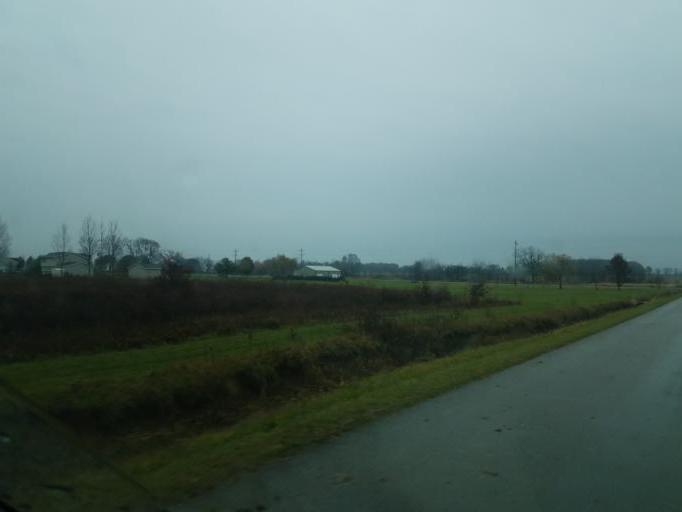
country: US
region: Ohio
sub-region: Knox County
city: Centerburg
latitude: 40.2473
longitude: -82.7369
